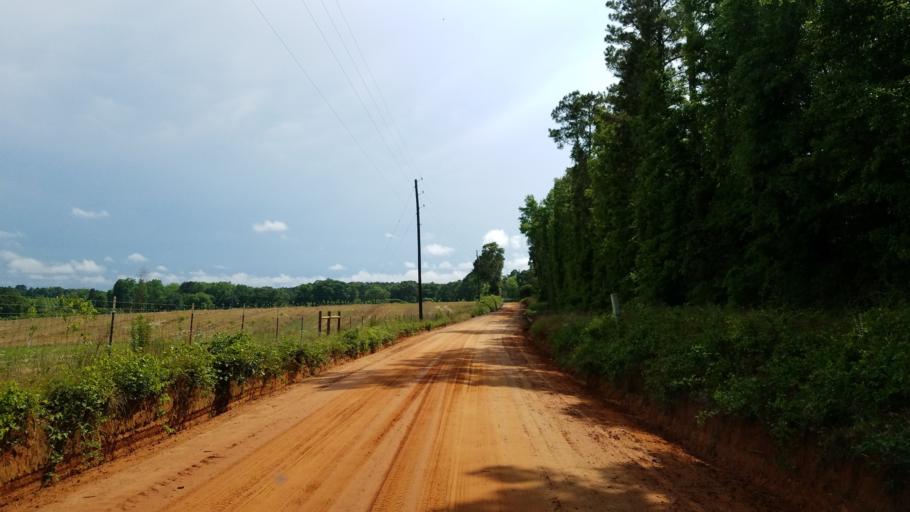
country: US
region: Georgia
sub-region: Houston County
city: Perry
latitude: 32.4502
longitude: -83.7854
